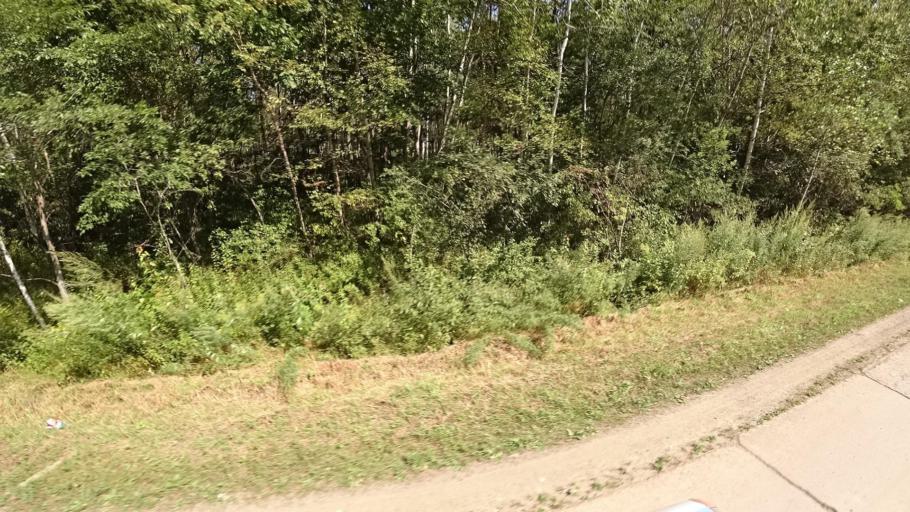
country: RU
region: Khabarovsk Krai
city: Khor
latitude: 47.9870
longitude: 135.0959
